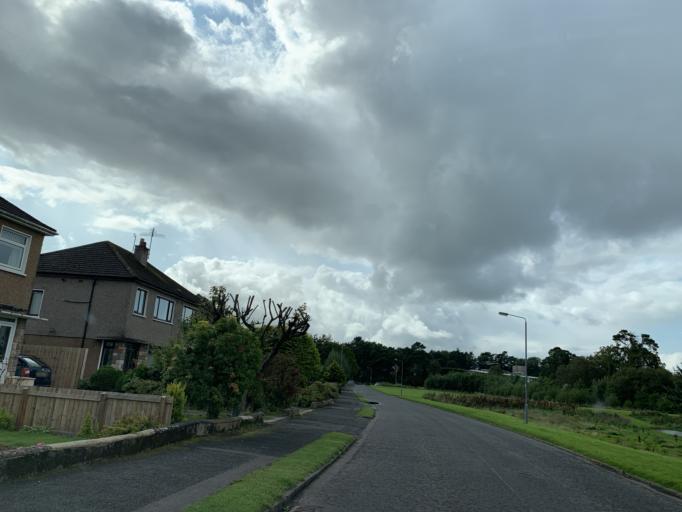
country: GB
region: Scotland
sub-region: East Renfrewshire
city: Newton Mearns
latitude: 55.7848
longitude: -4.3245
